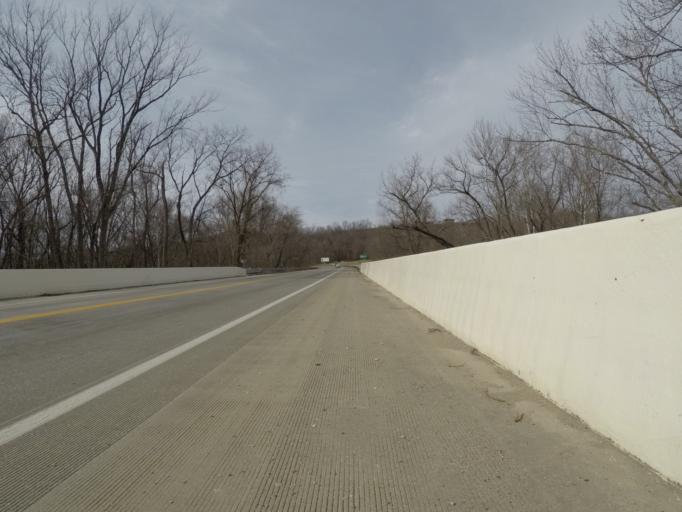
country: US
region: West Virginia
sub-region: Cabell County
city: Huntington
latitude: 38.4426
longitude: -82.3982
